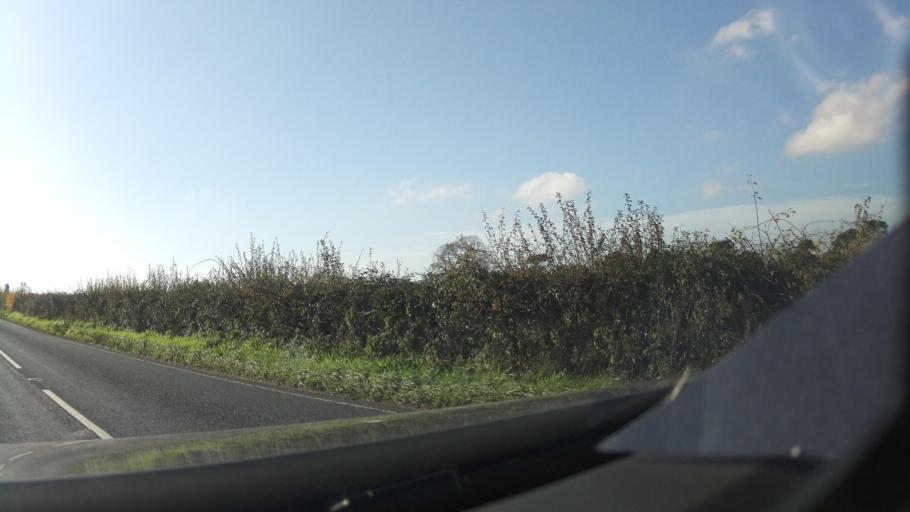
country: GB
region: England
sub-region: Somerset
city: Frome
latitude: 51.2062
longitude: -2.3172
